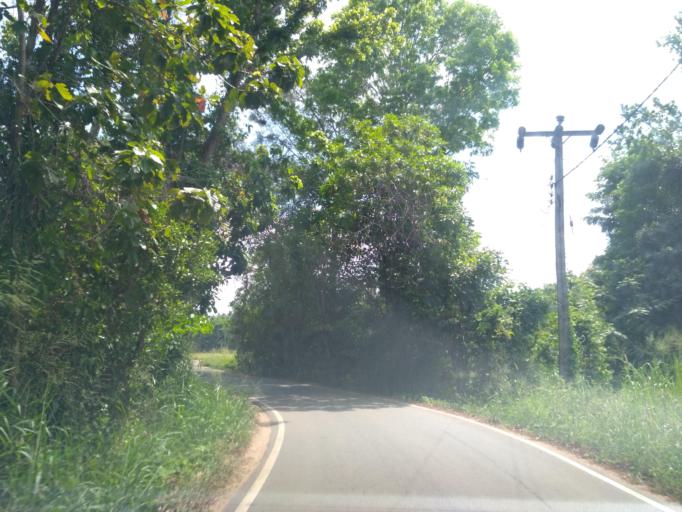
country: LK
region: North Western
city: Kuliyapitiya
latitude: 7.3325
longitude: 80.0630
